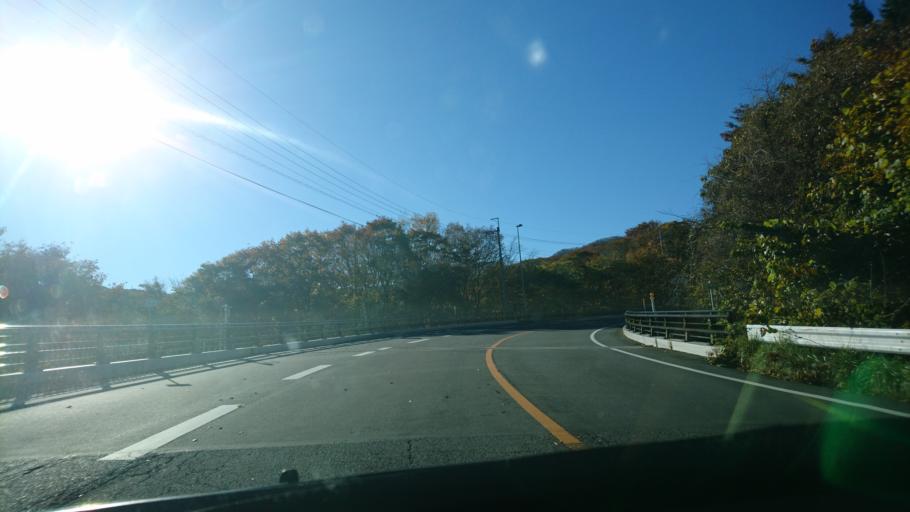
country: JP
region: Nagano
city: Saku
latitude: 36.3153
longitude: 138.6588
